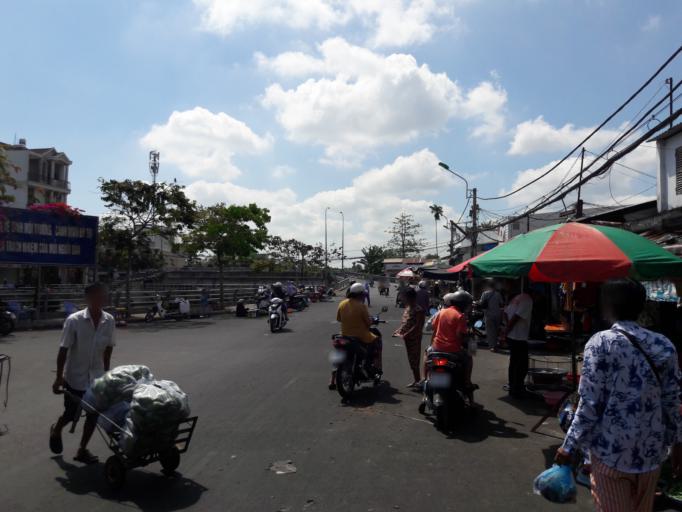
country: VN
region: Can Tho
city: Can Tho
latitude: 10.0261
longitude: 105.7773
